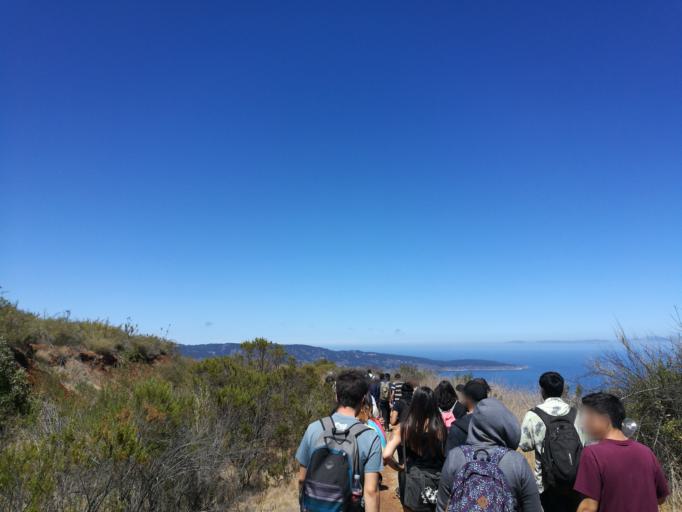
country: CL
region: Valparaiso
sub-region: Provincia de Valparaiso
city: Valparaiso
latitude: -33.0726
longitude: -71.6570
